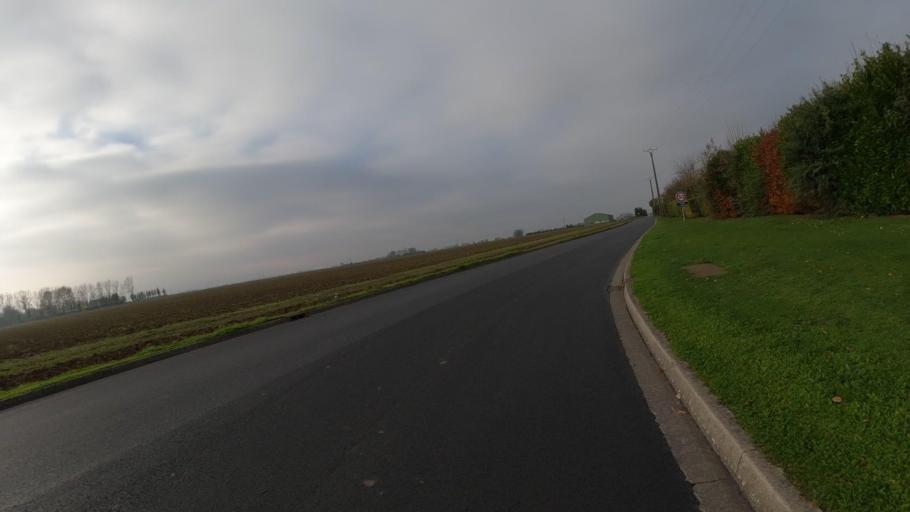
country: FR
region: Lower Normandy
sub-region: Departement du Calvados
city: Saint-Contest
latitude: 49.1999
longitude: -0.4135
